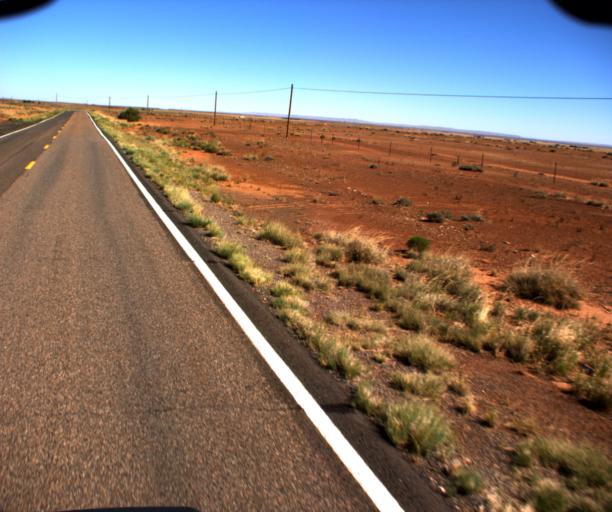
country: US
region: Arizona
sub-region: Coconino County
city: LeChee
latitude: 35.1457
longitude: -110.8941
